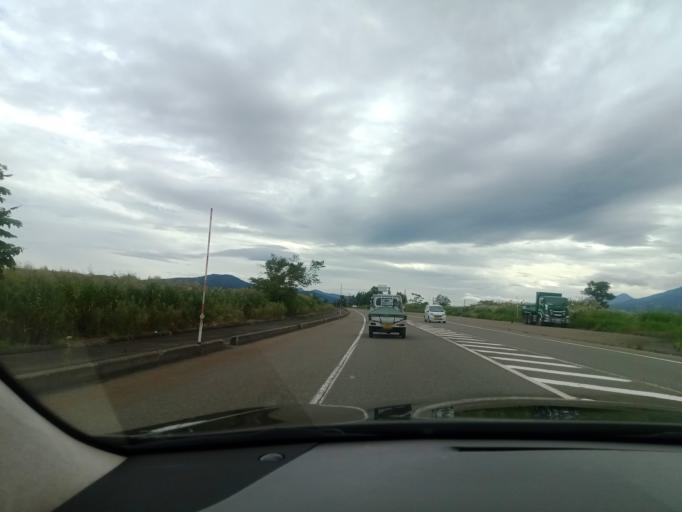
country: JP
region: Niigata
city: Arai
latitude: 37.0231
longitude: 138.2270
